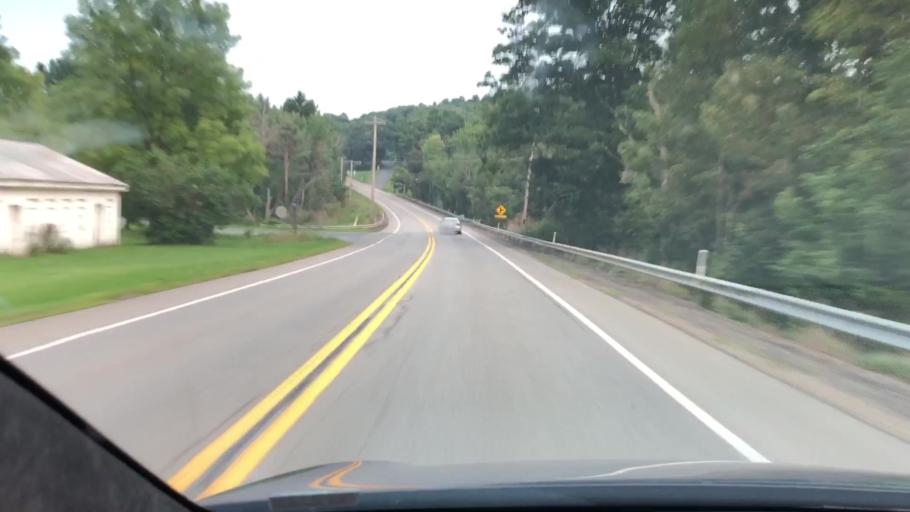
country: US
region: Pennsylvania
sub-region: Butler County
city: Slippery Rock
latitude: 41.0057
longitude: -79.9994
